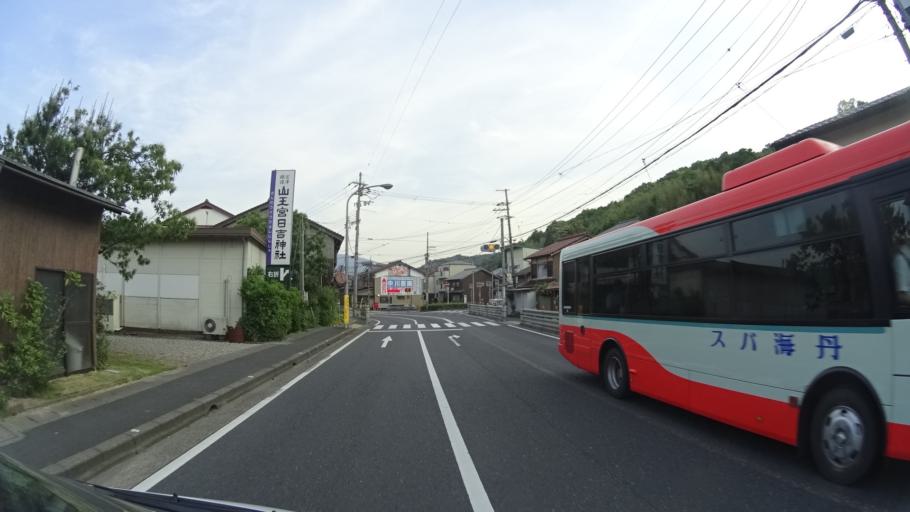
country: JP
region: Kyoto
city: Miyazu
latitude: 35.5437
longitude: 135.1901
